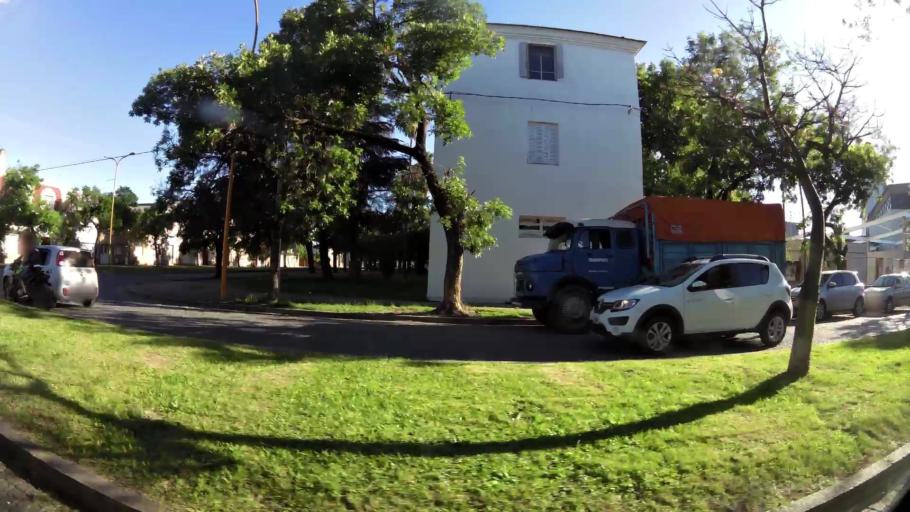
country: AR
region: Cordoba
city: San Francisco
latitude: -31.4356
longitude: -62.0856
